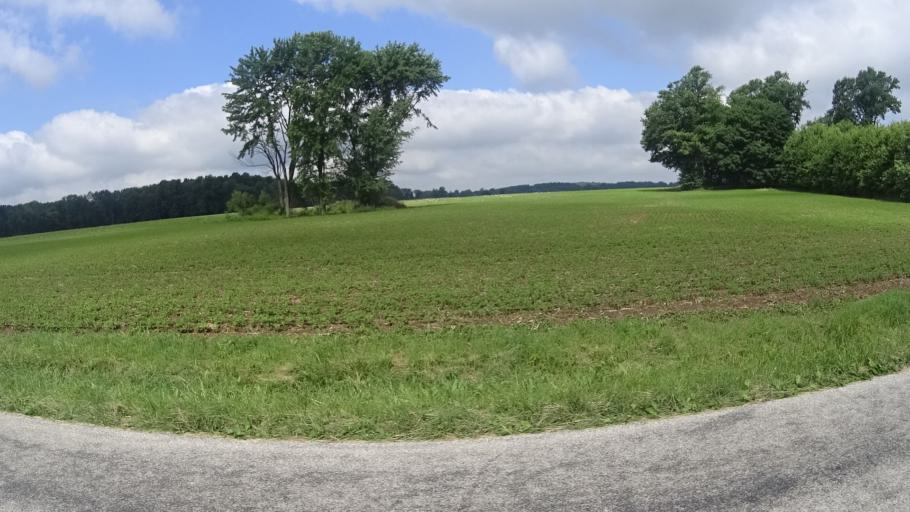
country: US
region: Ohio
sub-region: Huron County
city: Wakeman
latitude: 41.3254
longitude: -82.4511
